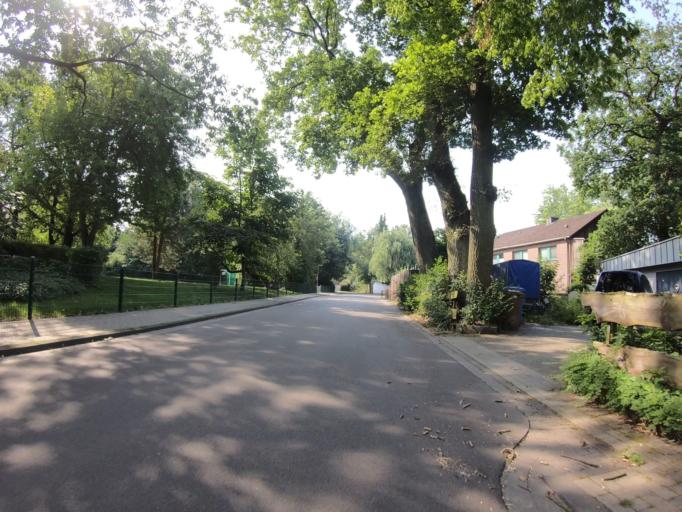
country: DE
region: Lower Saxony
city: Gifhorn
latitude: 52.4826
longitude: 10.5364
